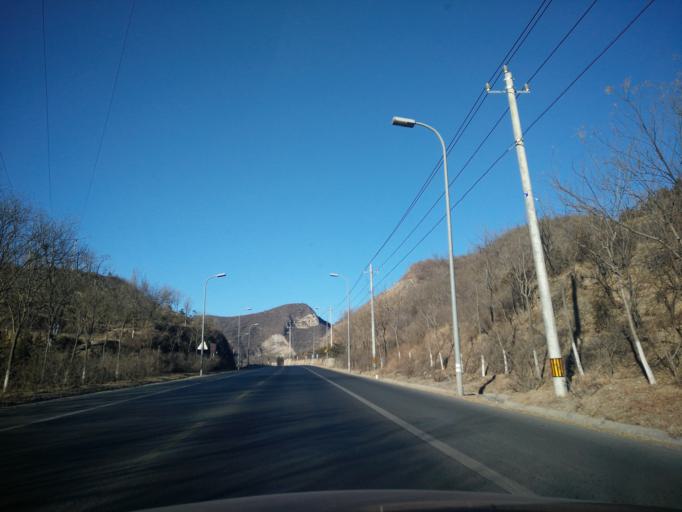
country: CN
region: Beijing
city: Junzhuang
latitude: 39.9911
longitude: 116.0733
